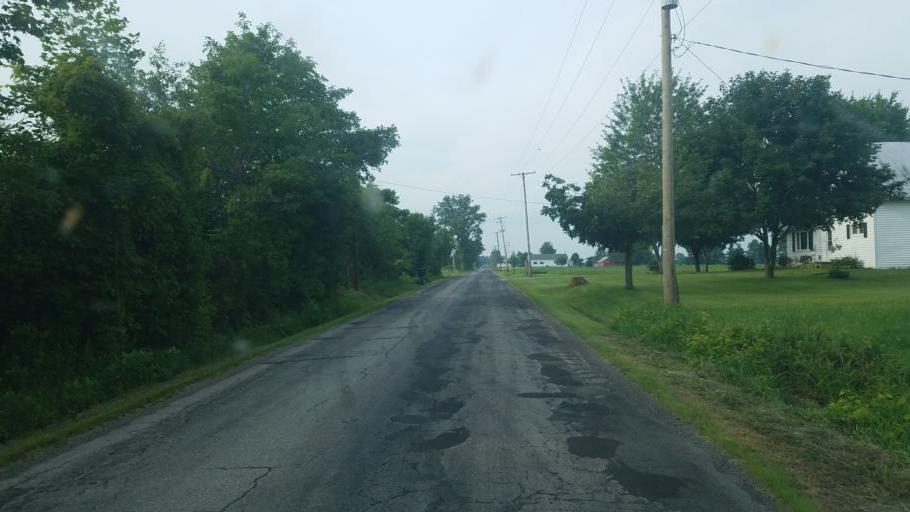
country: US
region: Ohio
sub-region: Morrow County
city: Cardington
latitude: 40.4774
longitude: -82.8955
